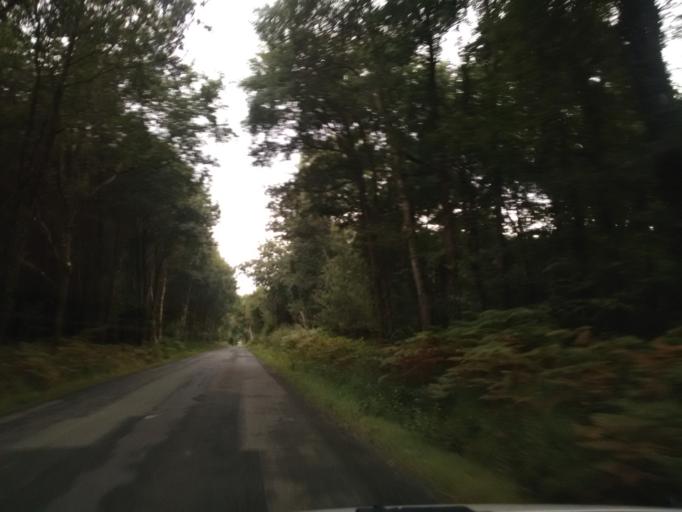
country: FR
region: Brittany
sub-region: Departement d'Ille-et-Vilaine
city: Dinge
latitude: 48.3523
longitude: -1.7652
